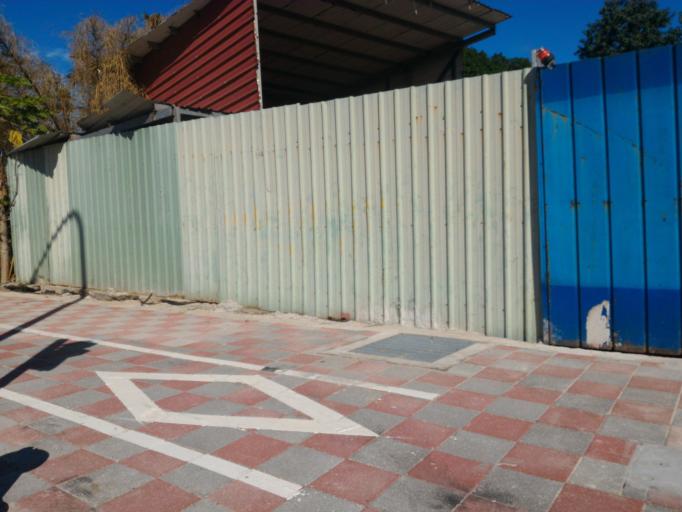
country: TW
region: Taiwan
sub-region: Taoyuan
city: Taoyuan
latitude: 24.9352
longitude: 121.3904
